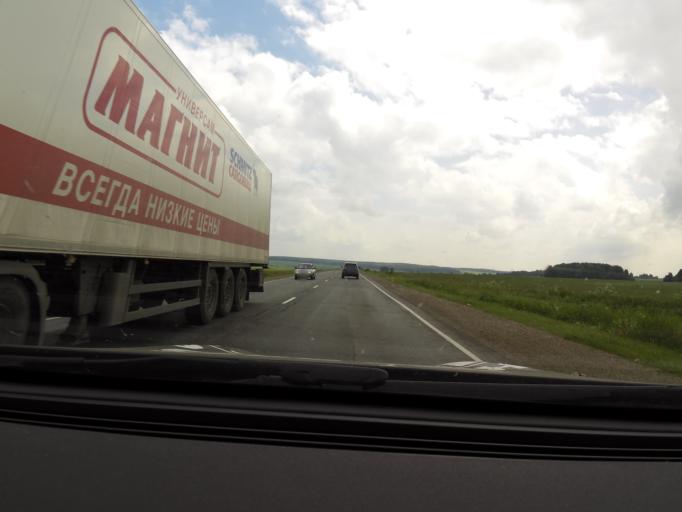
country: RU
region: Perm
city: Suksun
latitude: 56.9034
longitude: 57.5962
